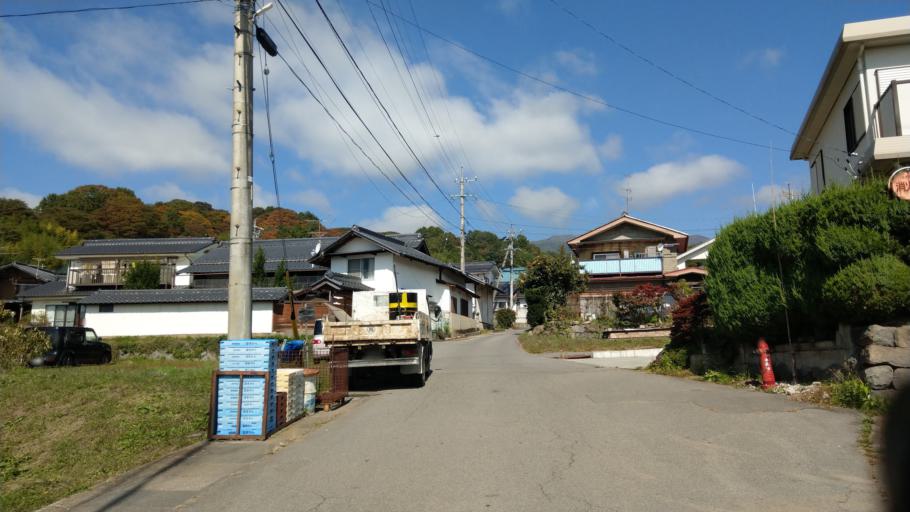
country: JP
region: Nagano
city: Komoro
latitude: 36.3513
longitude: 138.4313
